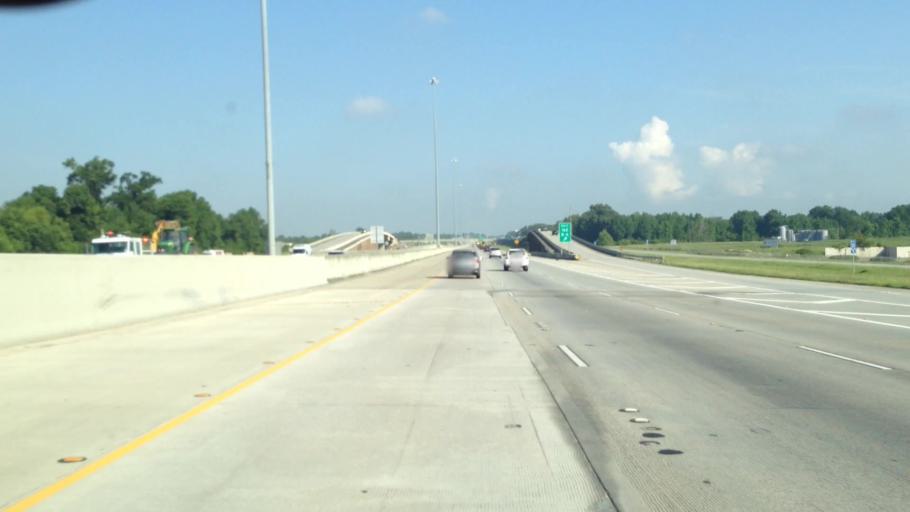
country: US
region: Louisiana
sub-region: East Baton Rouge Parish
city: Village Saint George
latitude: 30.3839
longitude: -91.0684
